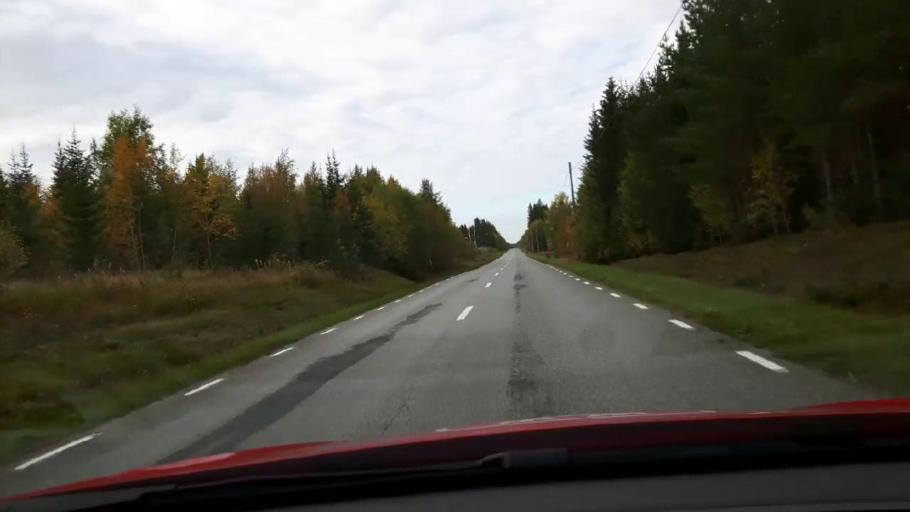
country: SE
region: Jaemtland
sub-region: Krokoms Kommun
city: Krokom
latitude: 63.1863
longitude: 14.0698
